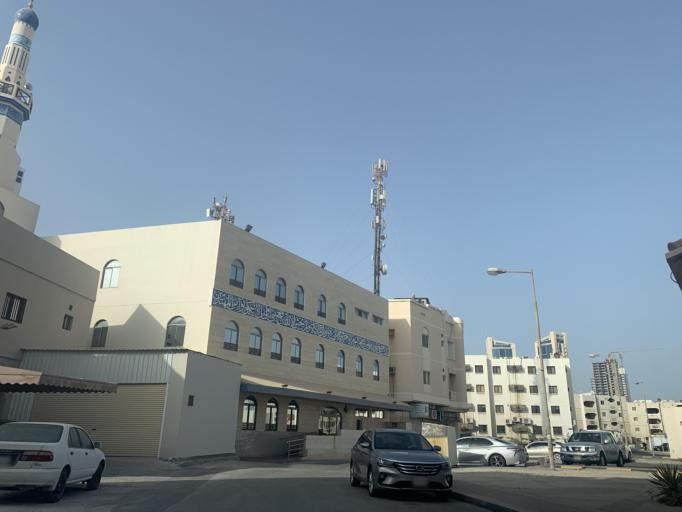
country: BH
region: Manama
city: Jidd Hafs
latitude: 26.2274
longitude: 50.5491
